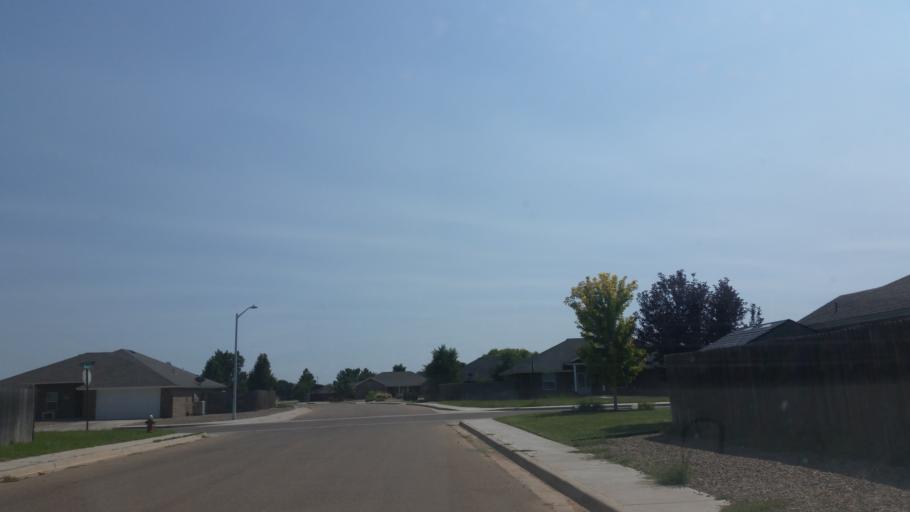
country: US
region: New Mexico
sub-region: Curry County
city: Clovis
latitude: 34.4447
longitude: -103.1762
